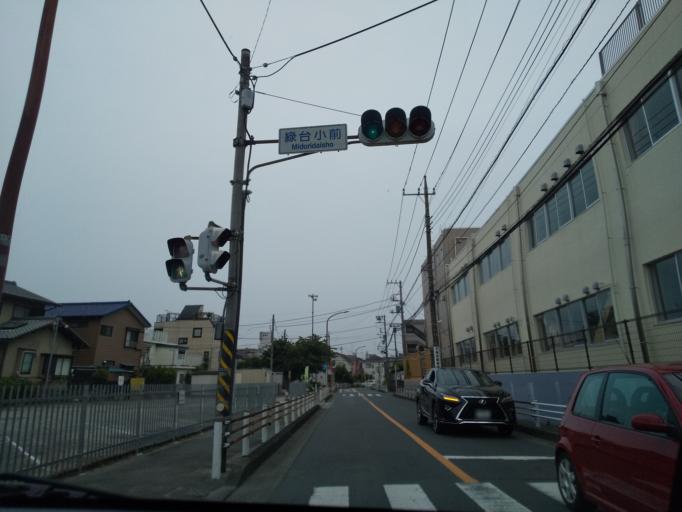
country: JP
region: Kanagawa
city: Zama
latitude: 35.5054
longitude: 139.4046
